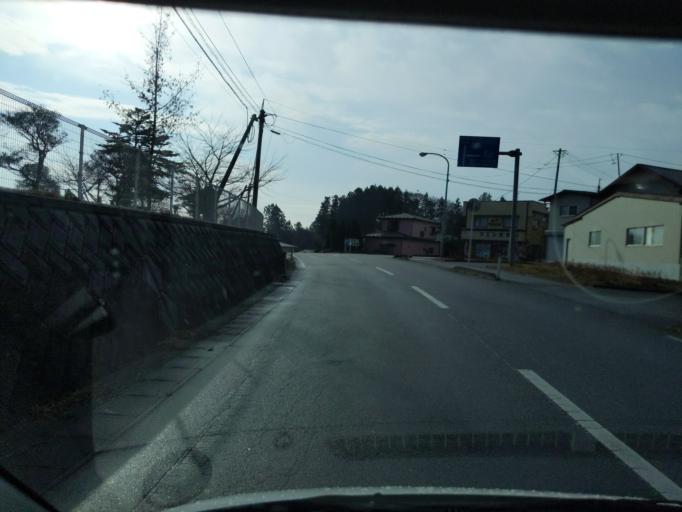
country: JP
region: Miyagi
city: Wakuya
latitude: 38.7010
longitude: 141.1593
